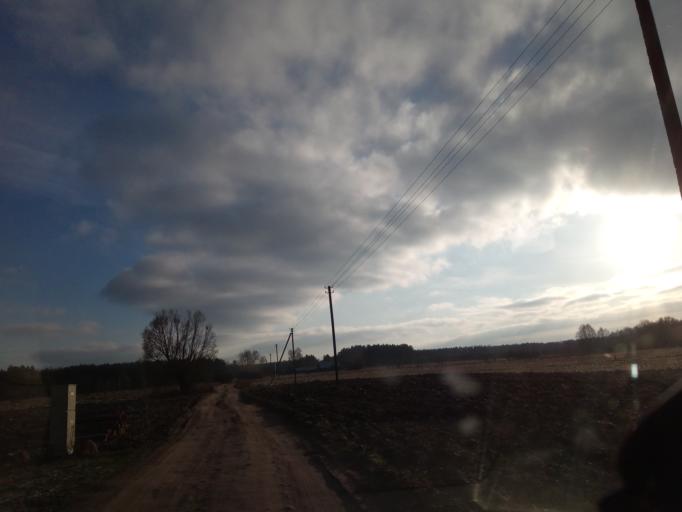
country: LT
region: Alytaus apskritis
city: Druskininkai
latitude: 53.9799
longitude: 24.2415
